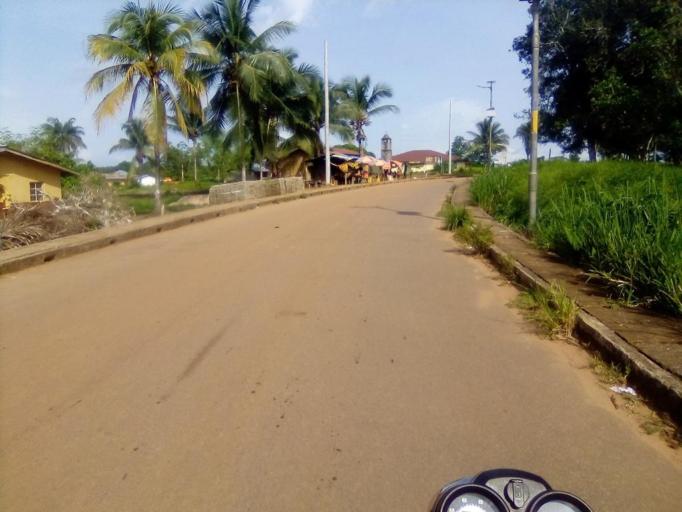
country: SL
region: Southern Province
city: Pujehun
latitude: 7.3596
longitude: -11.7287
